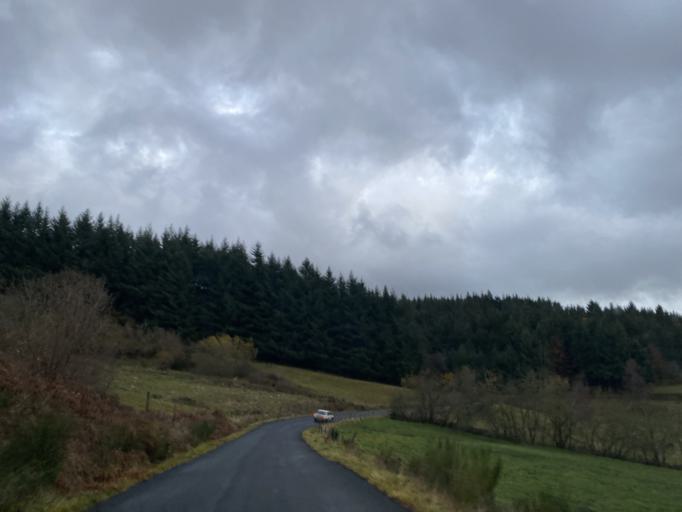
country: FR
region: Auvergne
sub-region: Departement du Puy-de-Dome
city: Cunlhat
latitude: 45.5768
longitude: 3.5600
